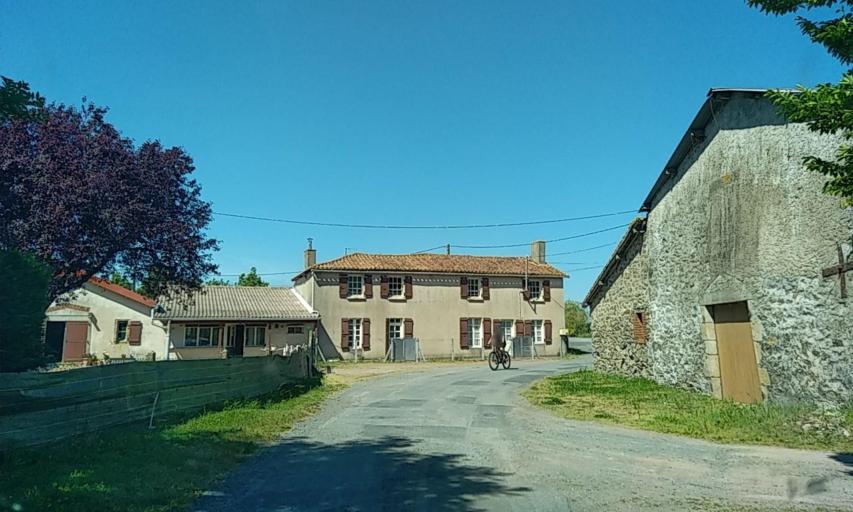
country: FR
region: Poitou-Charentes
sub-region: Departement des Deux-Sevres
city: La Chapelle-Saint-Laurent
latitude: 46.7689
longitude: -0.4660
